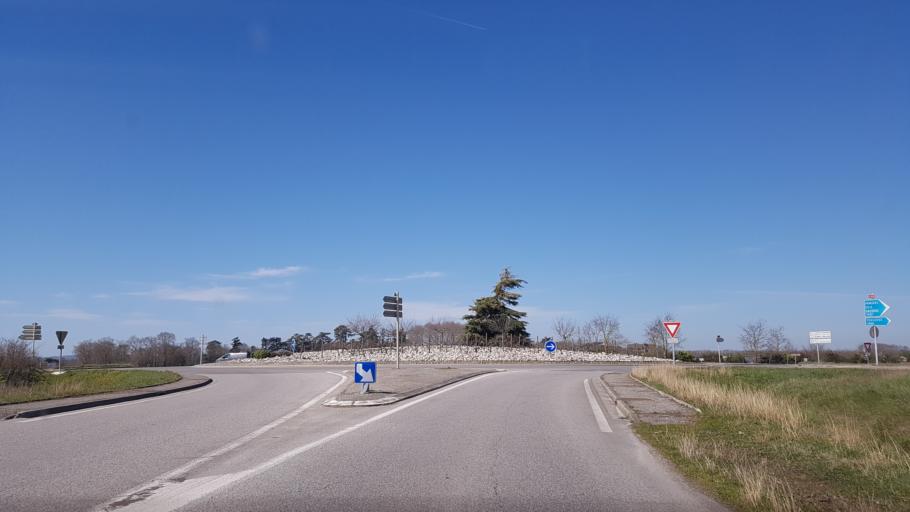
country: FR
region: Midi-Pyrenees
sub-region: Departement de l'Ariege
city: Mazeres
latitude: 43.2328
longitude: 1.6342
